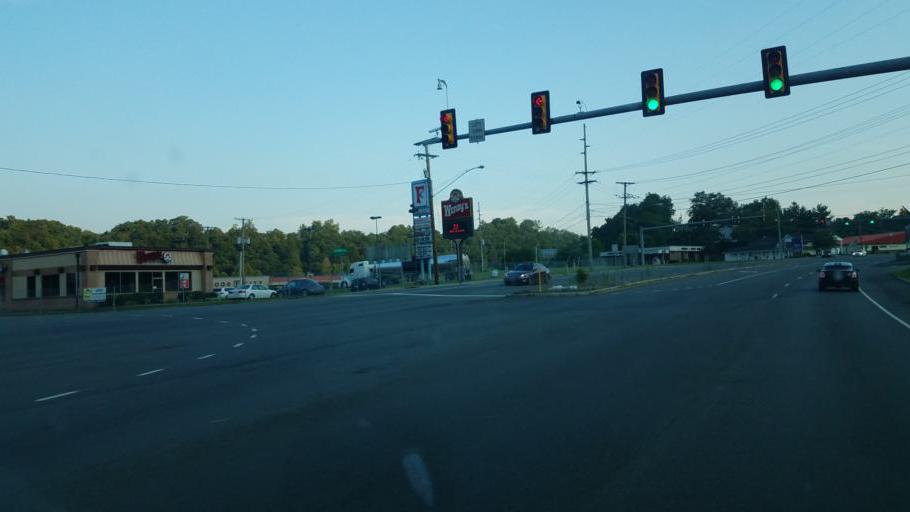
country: US
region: Virginia
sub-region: Scott County
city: Weber City
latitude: 36.6312
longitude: -82.5525
